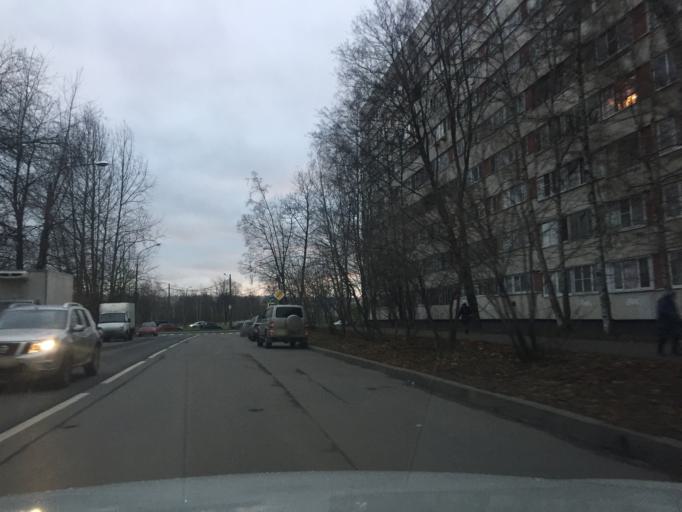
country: RU
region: St.-Petersburg
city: Grazhdanka
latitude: 60.0230
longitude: 30.4269
